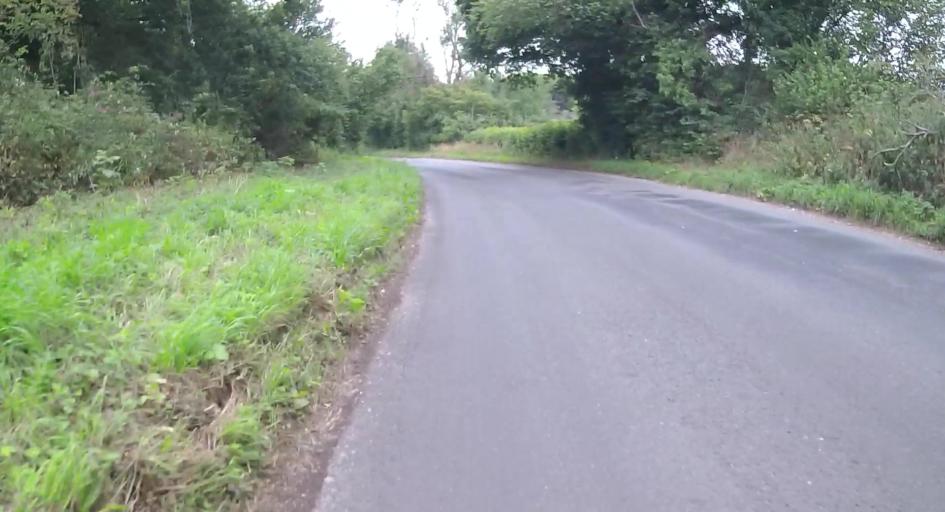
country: GB
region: England
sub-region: Hampshire
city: Bishops Waltham
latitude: 51.0264
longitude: -1.2032
